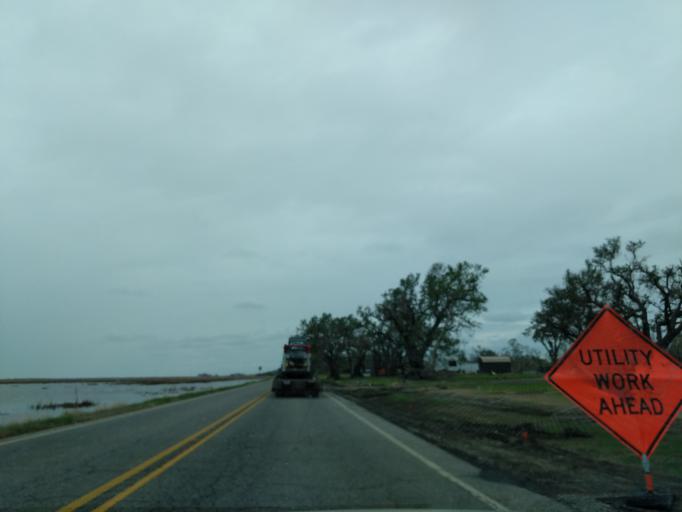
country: US
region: Louisiana
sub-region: Cameron Parish
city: Cameron
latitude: 29.7850
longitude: -93.0975
